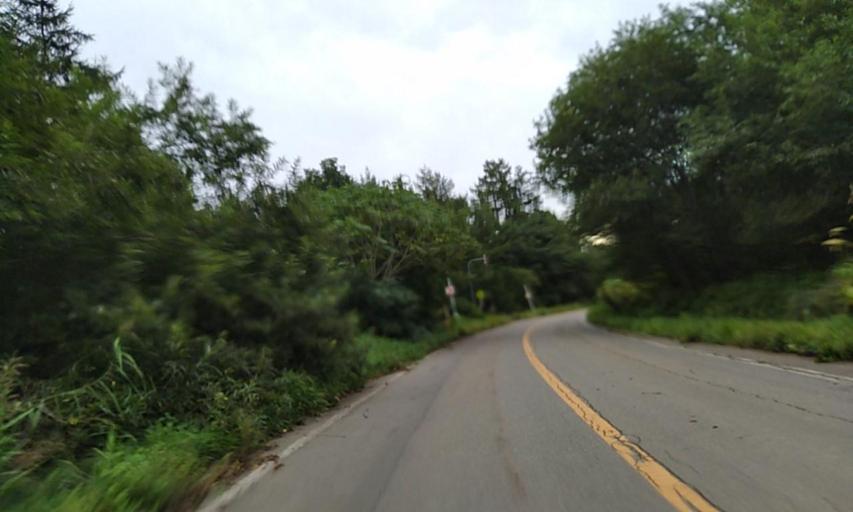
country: JP
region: Hokkaido
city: Obihiro
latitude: 42.6614
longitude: 143.0761
